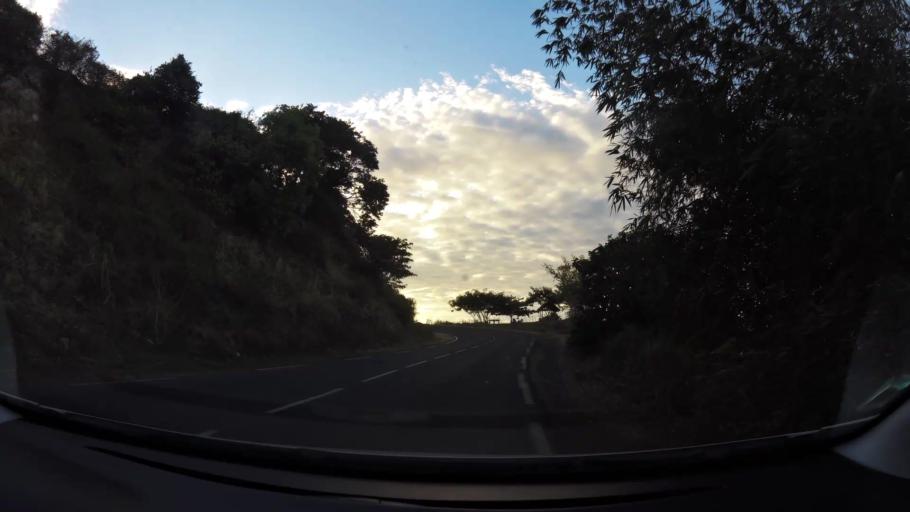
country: YT
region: Koungou
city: Koungou
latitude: -12.7312
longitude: 45.1981
